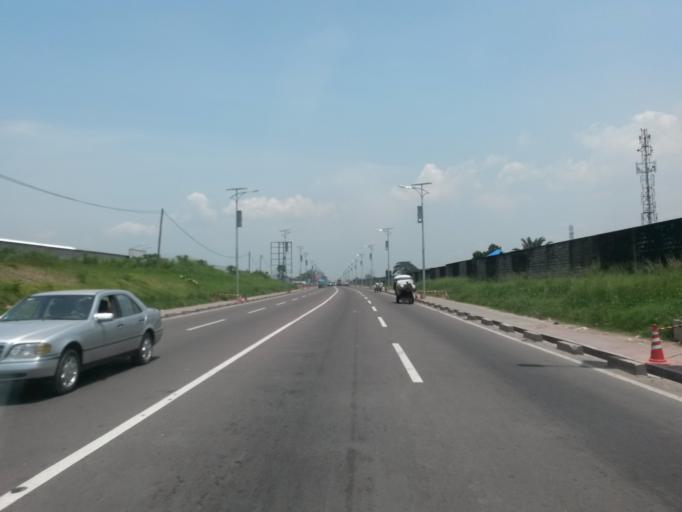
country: CD
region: Kinshasa
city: Kinshasa
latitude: -4.3189
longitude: 15.3343
